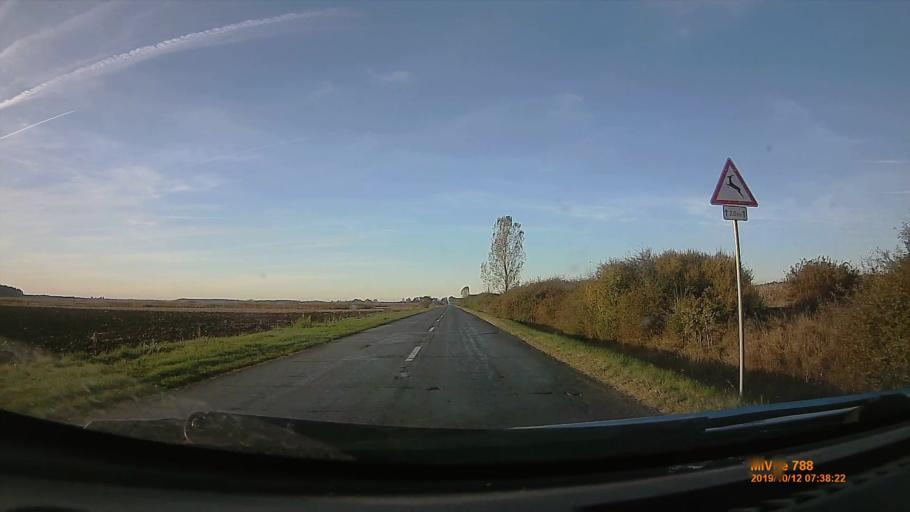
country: HU
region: Hajdu-Bihar
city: Pocsaj
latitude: 47.2258
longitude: 21.8104
